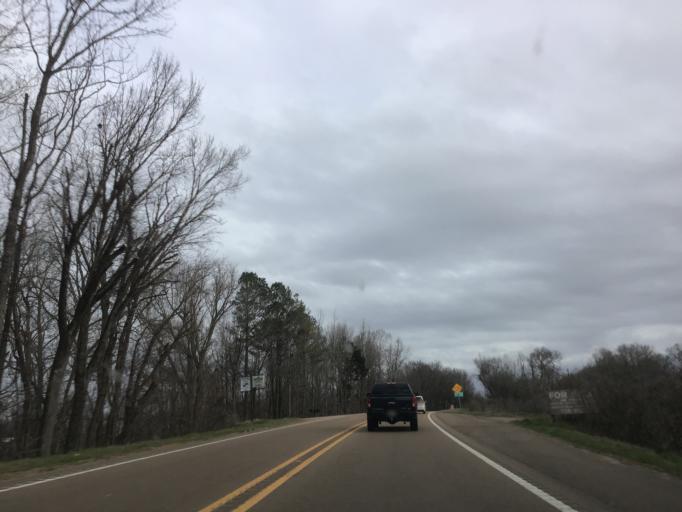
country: US
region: Mississippi
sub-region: Warren County
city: Beechwood
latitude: 32.3291
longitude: -90.8184
